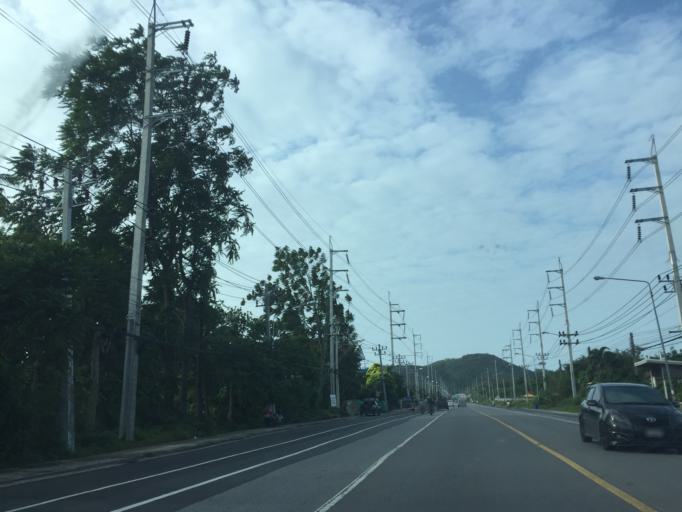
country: TH
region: Phuket
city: Mueang Phuket
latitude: 7.8562
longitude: 98.3804
